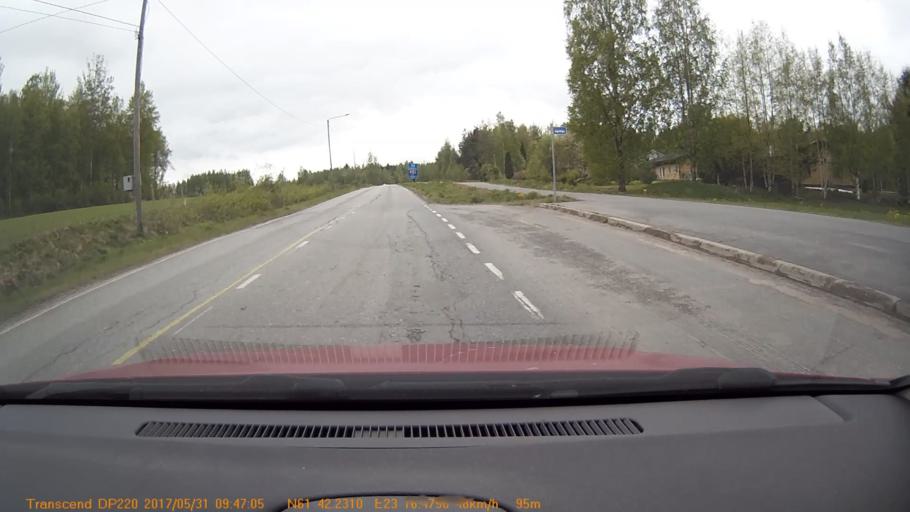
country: FI
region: Pirkanmaa
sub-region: Tampere
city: Viljakkala
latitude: 61.7039
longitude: 23.2750
